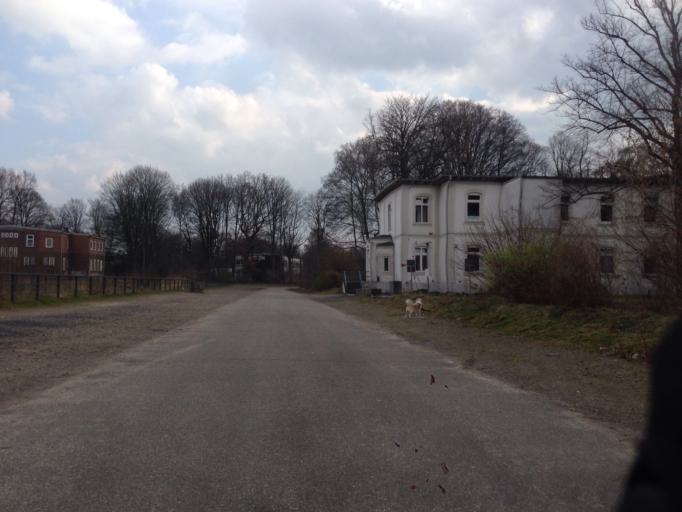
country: DE
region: Hamburg
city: Marienthal
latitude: 53.5784
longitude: 10.0555
